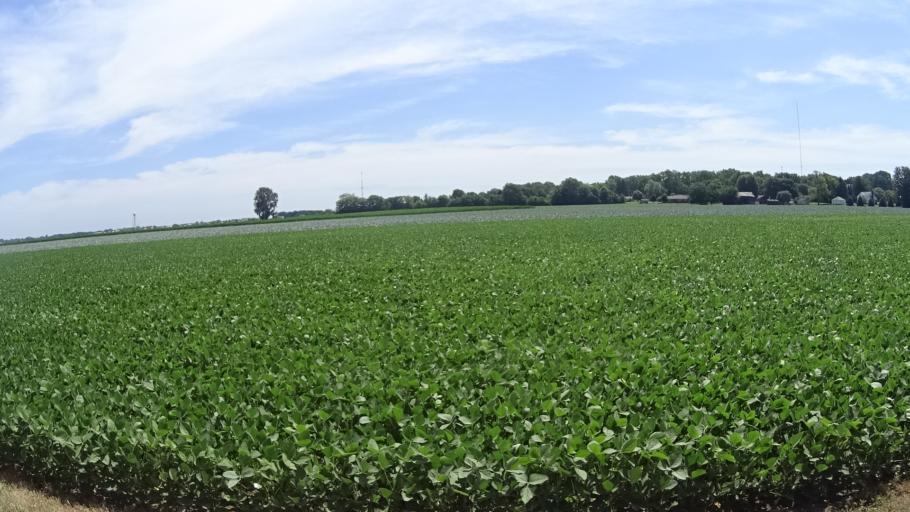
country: US
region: Ohio
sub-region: Erie County
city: Sandusky
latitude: 41.4043
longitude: -82.8044
